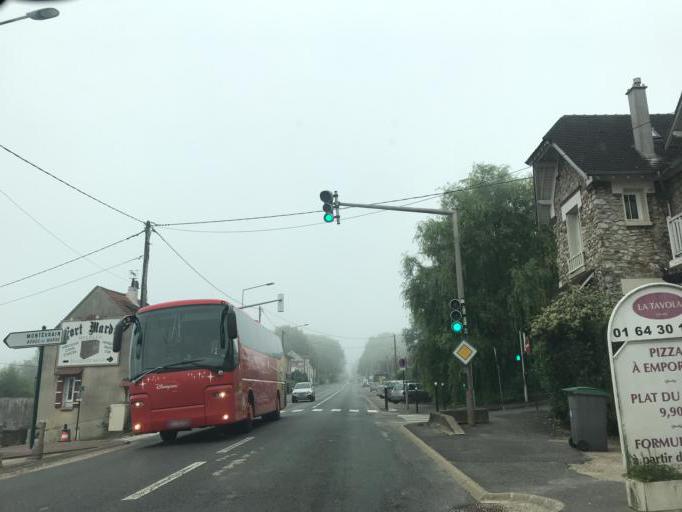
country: FR
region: Ile-de-France
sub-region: Departement de Seine-et-Marne
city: Montevrain
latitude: 48.8780
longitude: 2.7442
